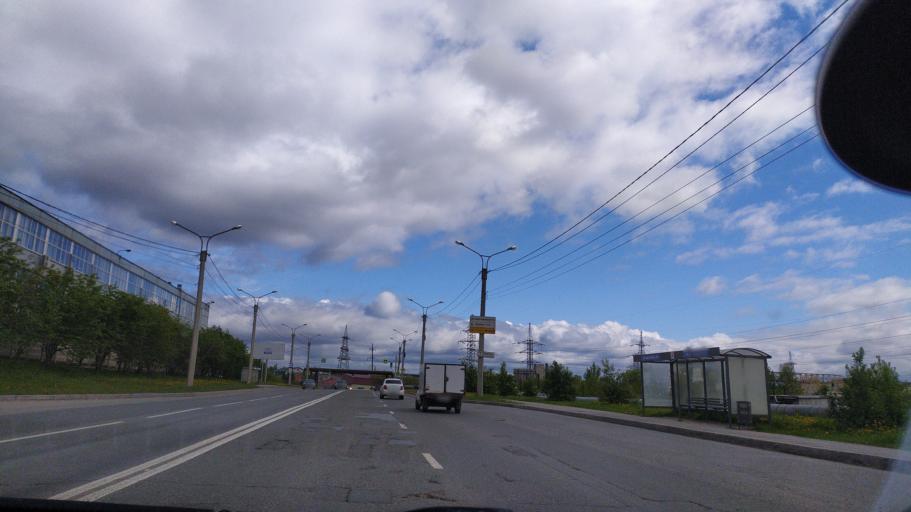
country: RU
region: Chuvashia
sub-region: Cheboksarskiy Rayon
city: Cheboksary
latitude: 56.1154
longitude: 47.2998
